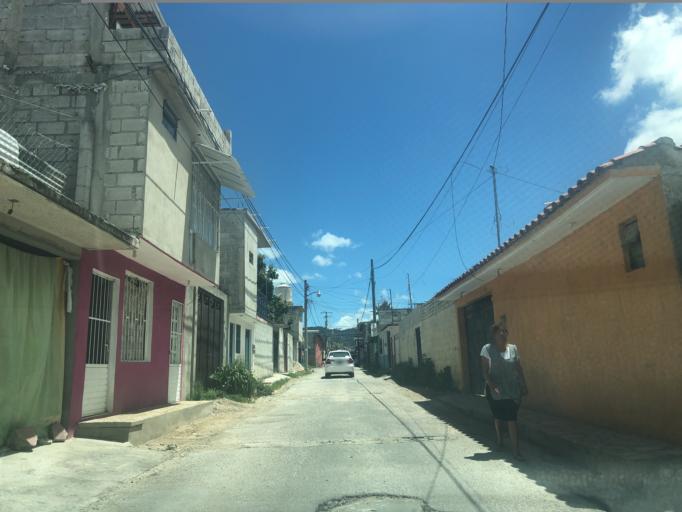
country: MX
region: Chiapas
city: San Cristobal de las Casas
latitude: 16.7176
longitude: -92.6444
